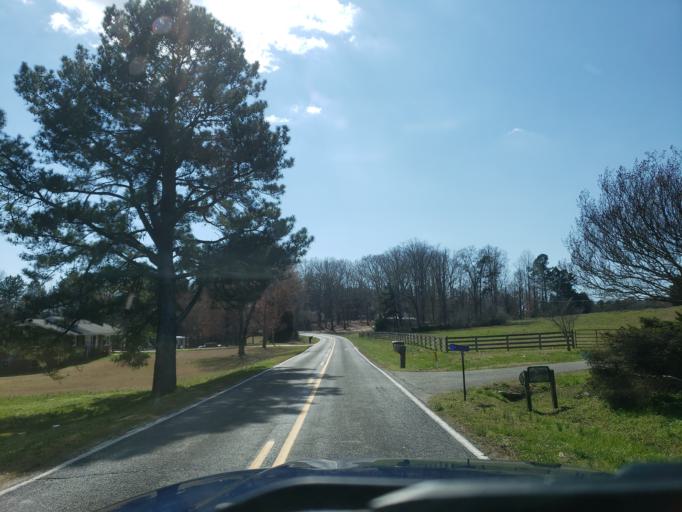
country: US
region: North Carolina
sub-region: Cleveland County
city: White Plains
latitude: 35.2306
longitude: -81.4010
